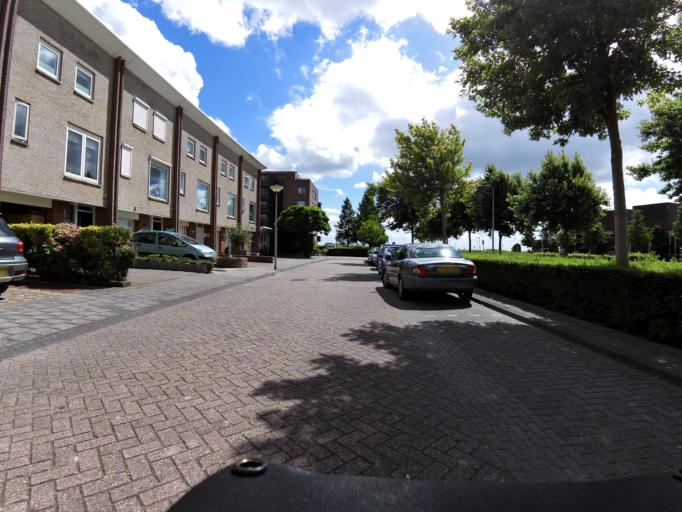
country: NL
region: South Holland
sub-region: Gemeente Oud-Beijerland
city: Oud-Beijerland
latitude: 51.8286
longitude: 4.3713
